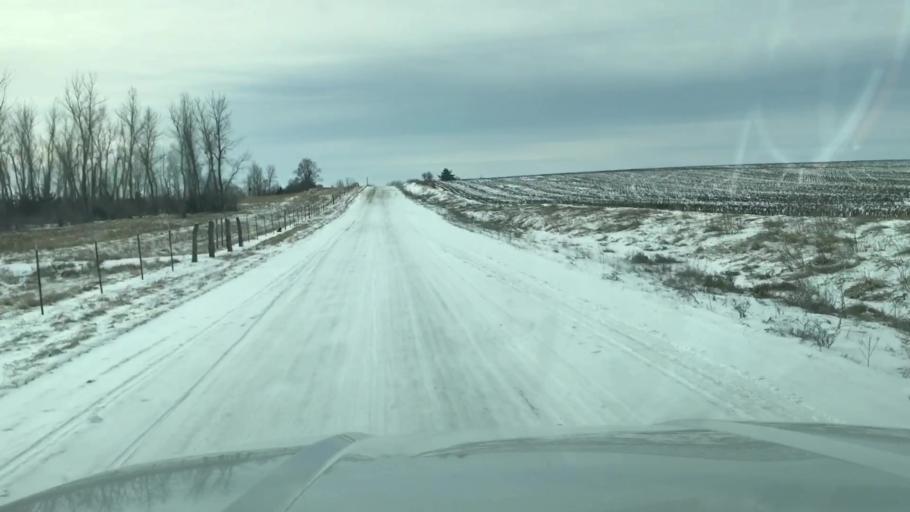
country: US
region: Missouri
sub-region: Holt County
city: Mound City
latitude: 40.1353
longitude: -95.0696
